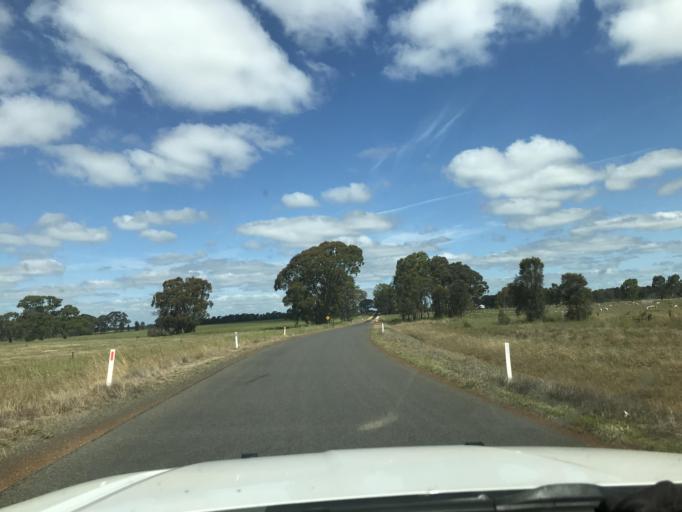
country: AU
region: South Australia
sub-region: Naracoorte and Lucindale
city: Naracoorte
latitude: -36.9929
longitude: 141.2913
